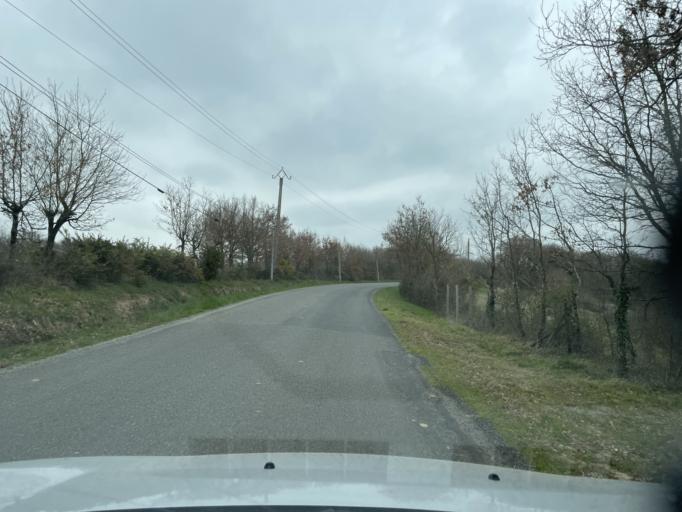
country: FR
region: Midi-Pyrenees
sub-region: Departement du Gers
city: Pujaudran
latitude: 43.5994
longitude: 1.1511
